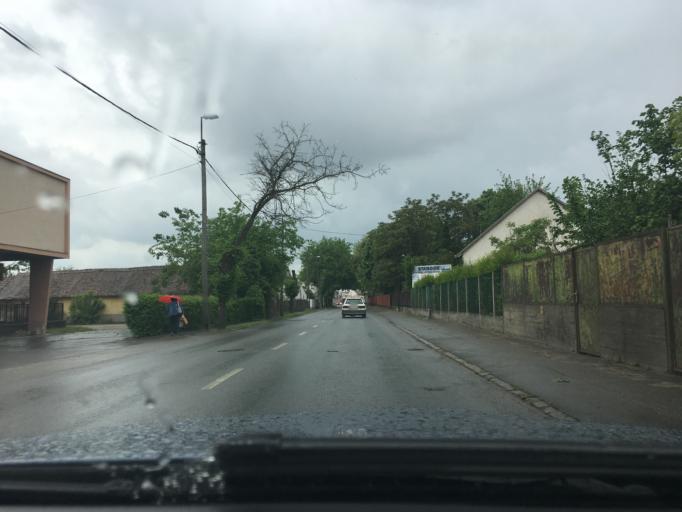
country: HU
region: Hajdu-Bihar
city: Debrecen
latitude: 47.5218
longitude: 21.6591
